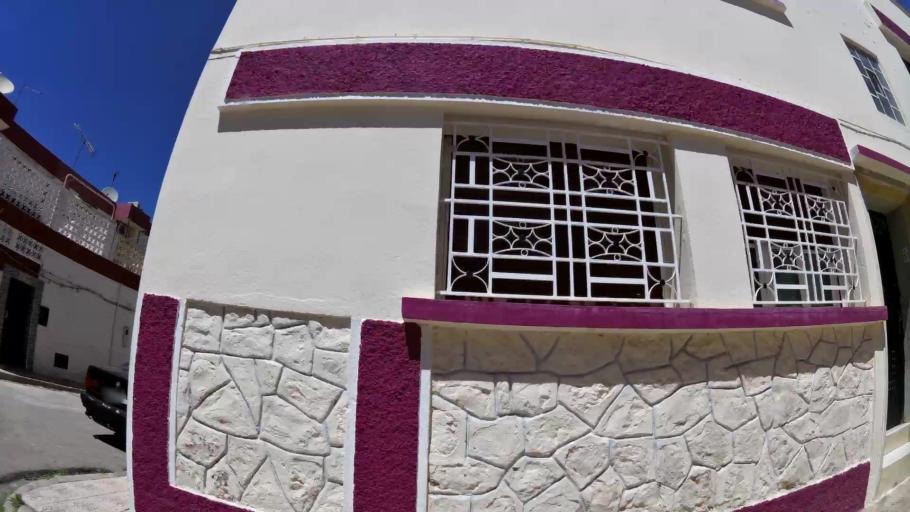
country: MA
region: Fes-Boulemane
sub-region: Fes
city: Fes
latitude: 34.0232
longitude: -5.0050
